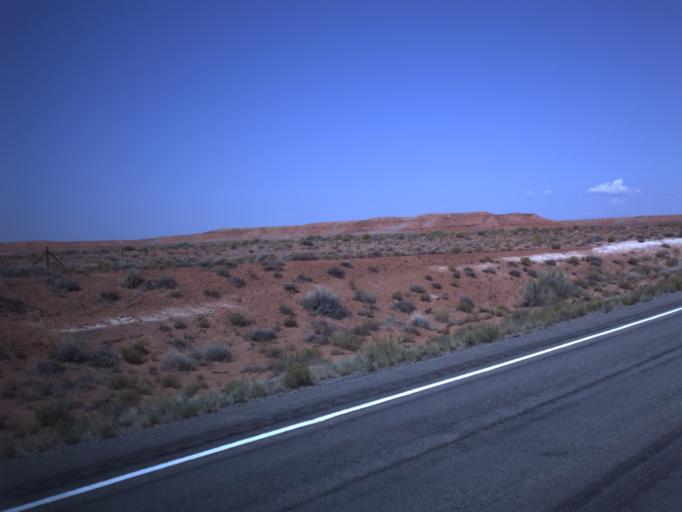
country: US
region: Utah
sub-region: San Juan County
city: Blanding
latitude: 37.0004
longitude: -109.6096
